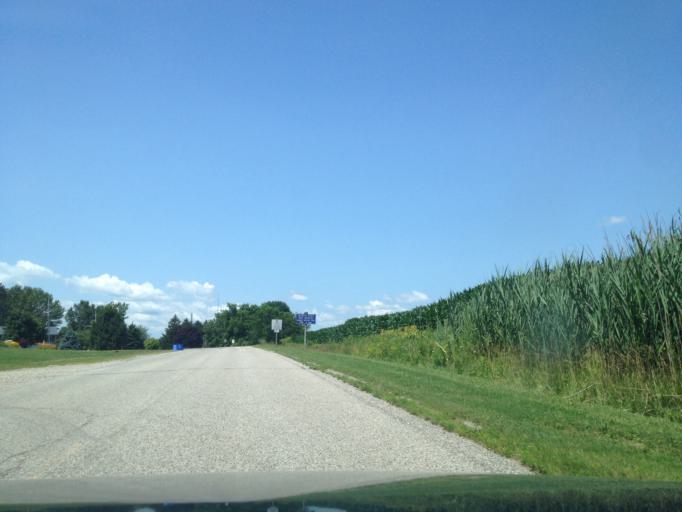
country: CA
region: Ontario
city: Aylmer
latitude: 42.6458
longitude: -80.7949
